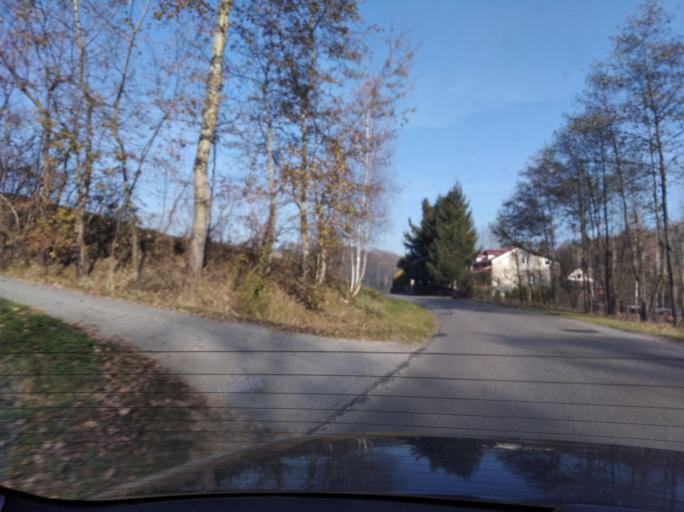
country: PL
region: Subcarpathian Voivodeship
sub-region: Powiat ropczycko-sedziszowski
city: Wielopole Skrzynskie
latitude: 49.9402
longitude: 21.5785
